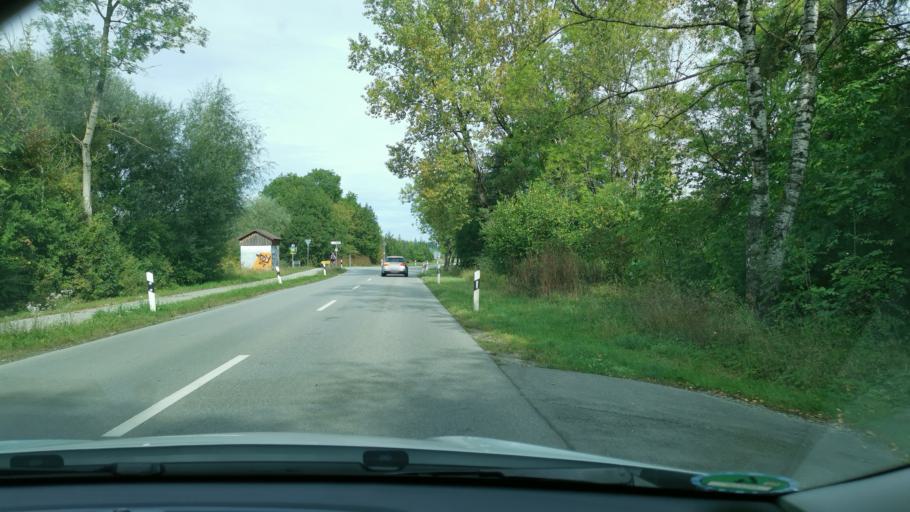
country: DE
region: Bavaria
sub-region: Upper Bavaria
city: Bergkirchen
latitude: 48.2401
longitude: 11.3579
